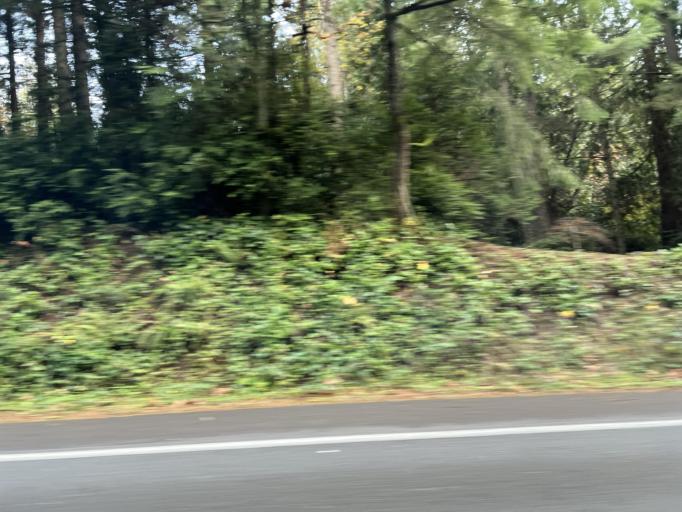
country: US
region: Washington
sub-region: Kitsap County
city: Bainbridge Island
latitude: 47.6613
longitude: -122.5188
